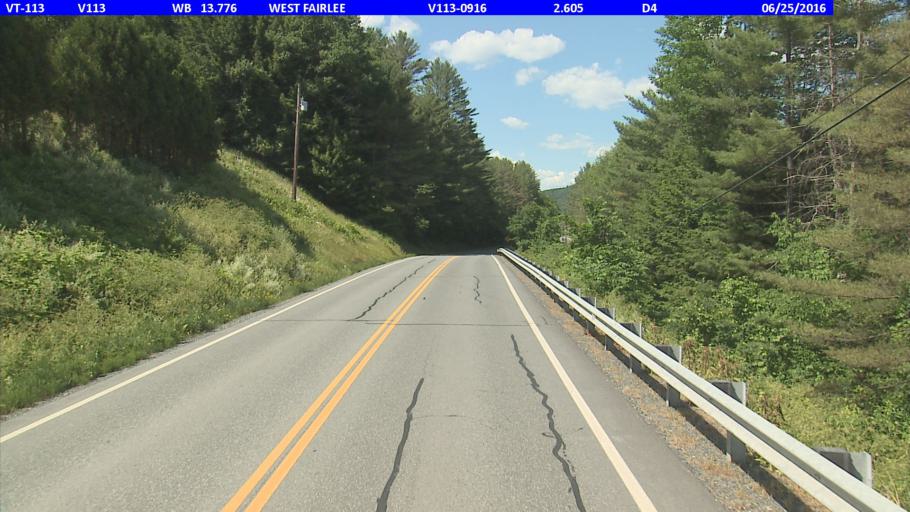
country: US
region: New Hampshire
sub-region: Grafton County
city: Orford
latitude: 43.9002
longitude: -72.2633
